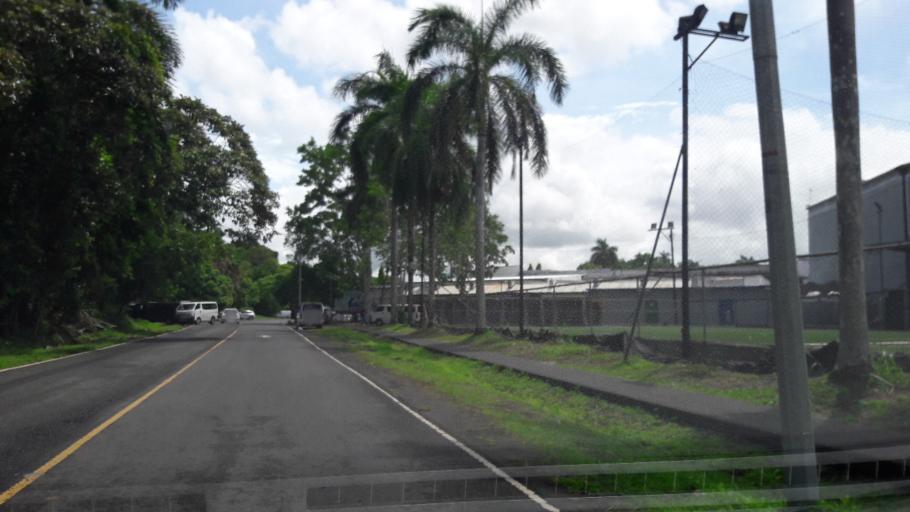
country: PA
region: Panama
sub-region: Distrito de Panama
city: Ancon
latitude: 8.9738
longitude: -79.5628
